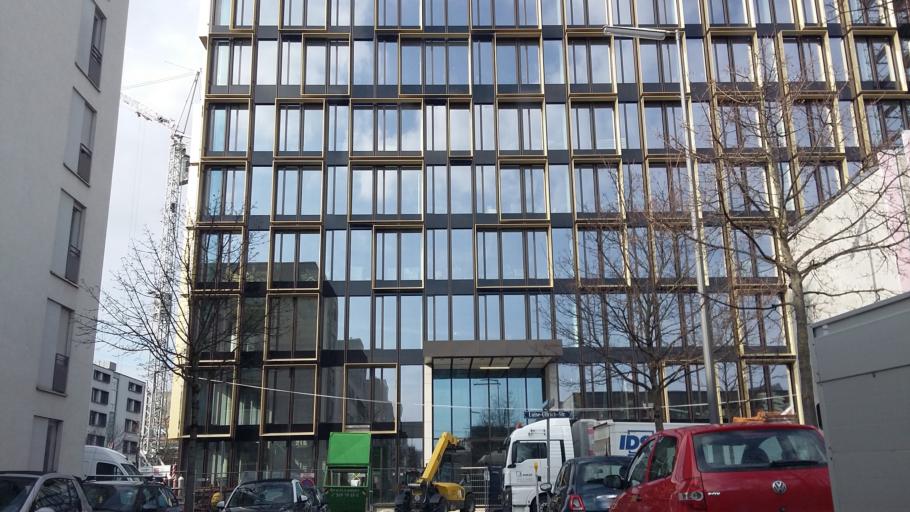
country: DE
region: Bavaria
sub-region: Upper Bavaria
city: Munich
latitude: 48.1445
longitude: 11.5389
